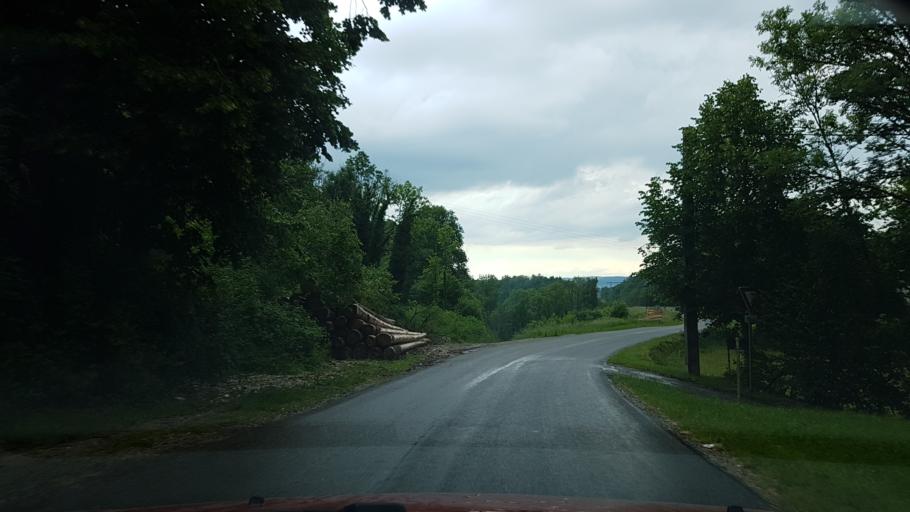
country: FR
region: Franche-Comte
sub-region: Departement du Jura
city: Clairvaux-les-Lacs
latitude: 46.5434
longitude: 5.7482
